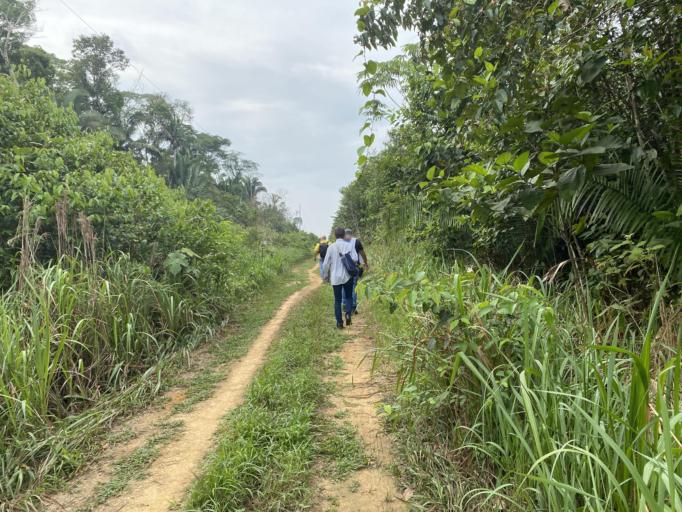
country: BR
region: Rondonia
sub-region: Porto Velho
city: Porto Velho
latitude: -8.8350
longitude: -64.2318
